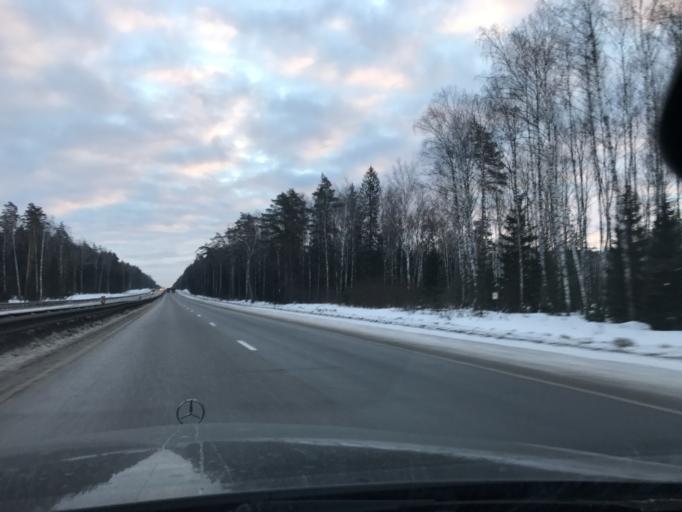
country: RU
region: Vladimir
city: Krasnyy Oktyabr'
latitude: 56.2202
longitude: 41.5005
